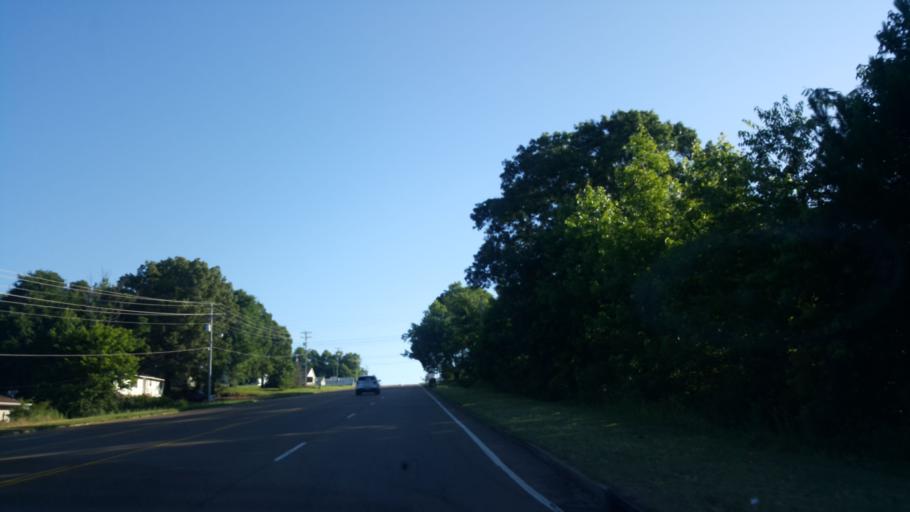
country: US
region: Tennessee
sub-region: Henderson County
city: Lexington
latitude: 35.6348
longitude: -88.4040
